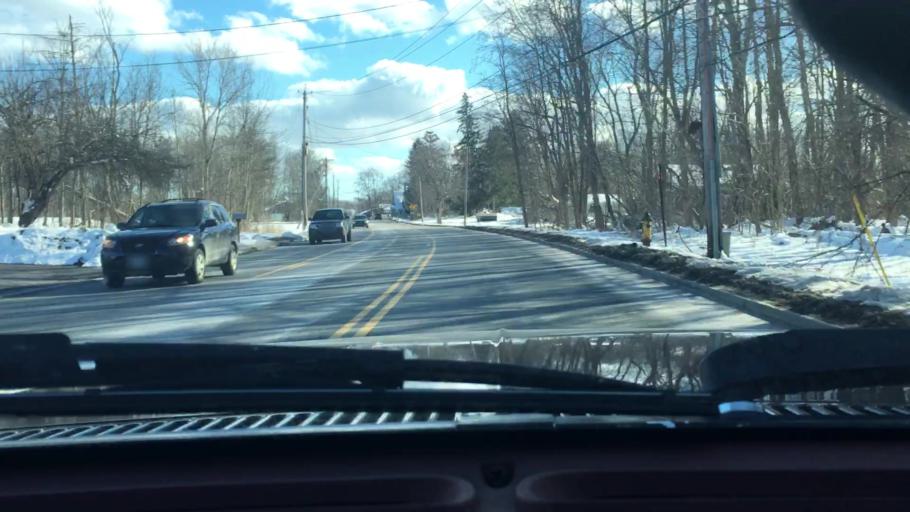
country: US
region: New York
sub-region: Onondaga County
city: Liverpool
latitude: 43.1903
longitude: -76.2170
